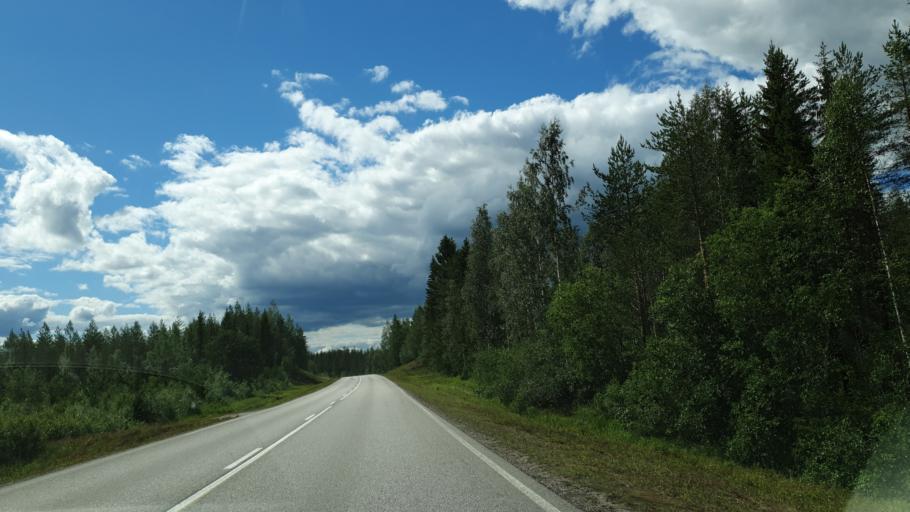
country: FI
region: Kainuu
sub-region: Kehys-Kainuu
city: Kuhmo
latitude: 63.8055
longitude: 29.4161
